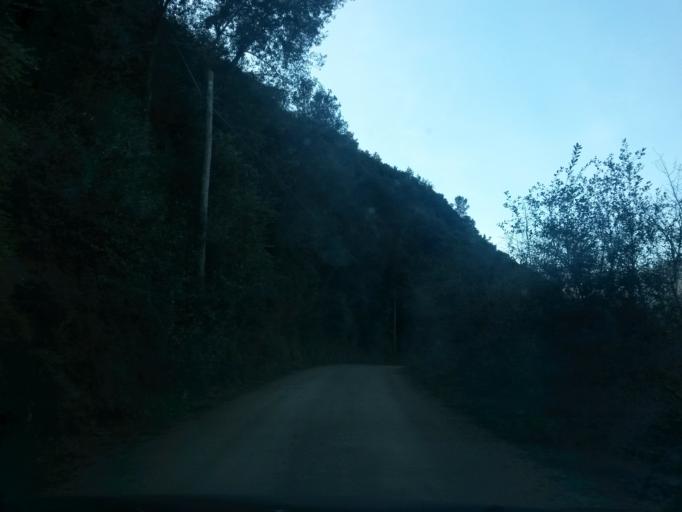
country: ES
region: Catalonia
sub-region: Provincia de Girona
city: la Cellera de Ter
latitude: 41.9775
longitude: 2.6302
